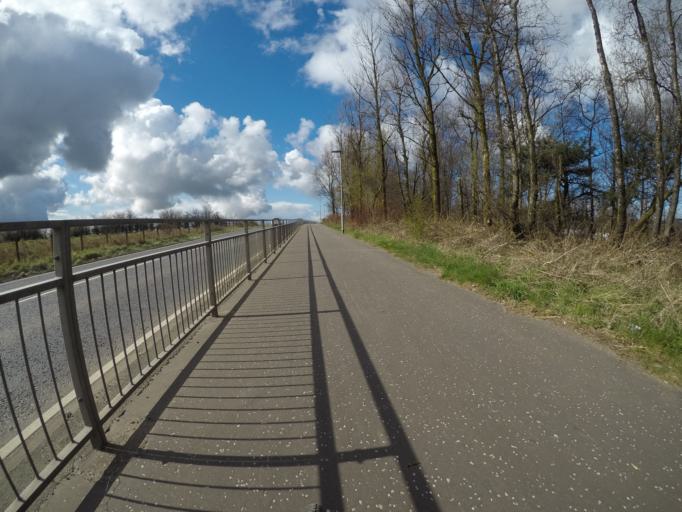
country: GB
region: Scotland
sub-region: North Ayrshire
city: Beith
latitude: 55.7425
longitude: -4.6508
